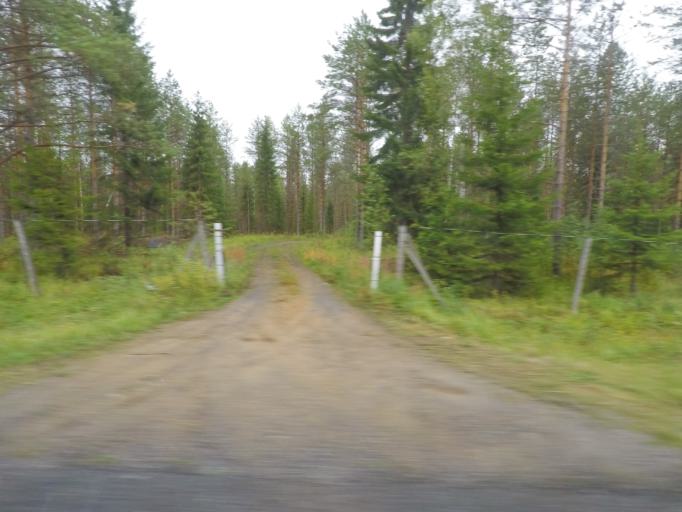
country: FI
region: Southern Savonia
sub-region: Pieksaemaeki
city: Juva
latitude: 61.9902
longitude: 27.8030
